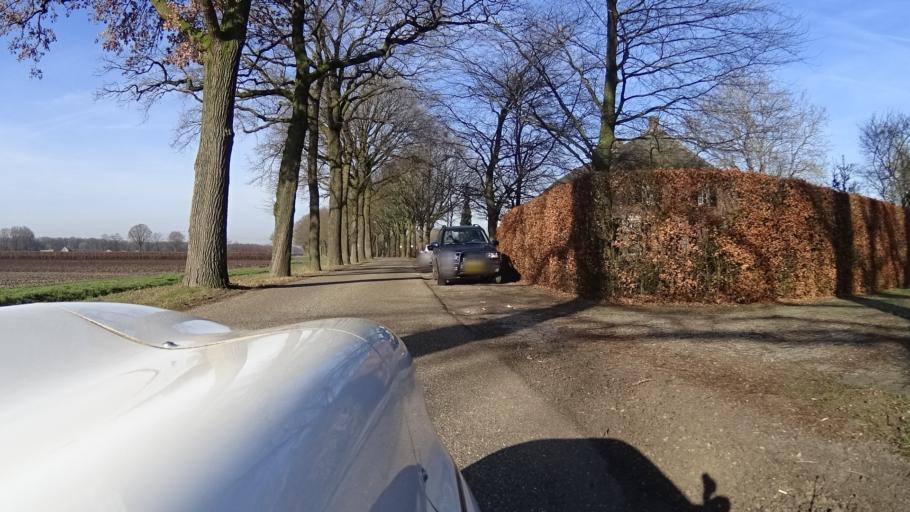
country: NL
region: North Brabant
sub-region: Gemeente Boekel
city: Boekel
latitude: 51.6020
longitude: 5.6571
